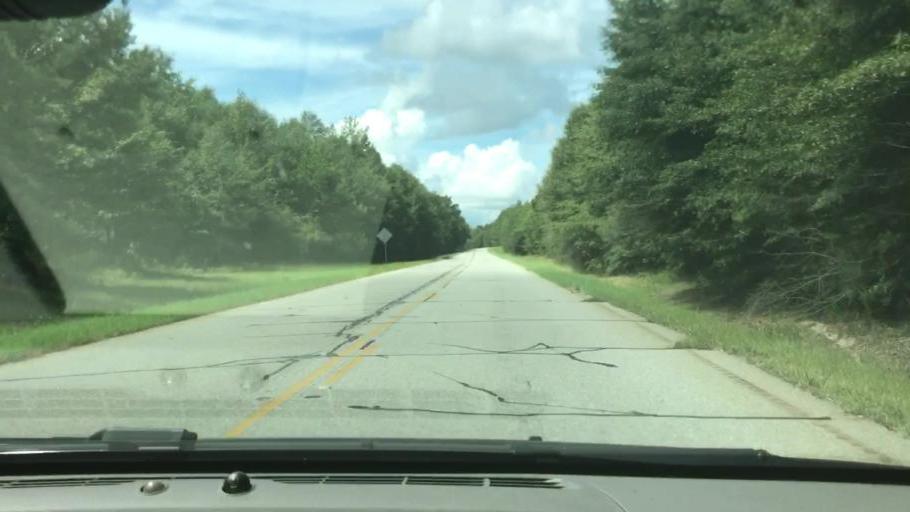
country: US
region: Georgia
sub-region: Stewart County
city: Lumpkin
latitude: 32.1388
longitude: -84.9632
